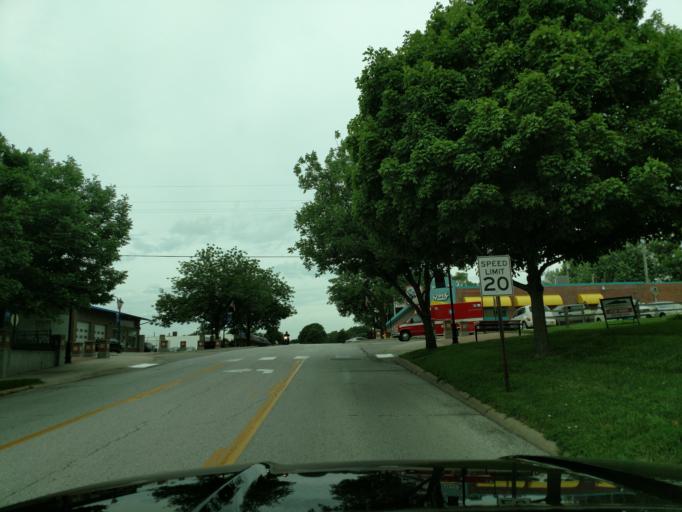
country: US
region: Nebraska
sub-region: Douglas County
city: Ralston
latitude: 41.2016
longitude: -96.0293
